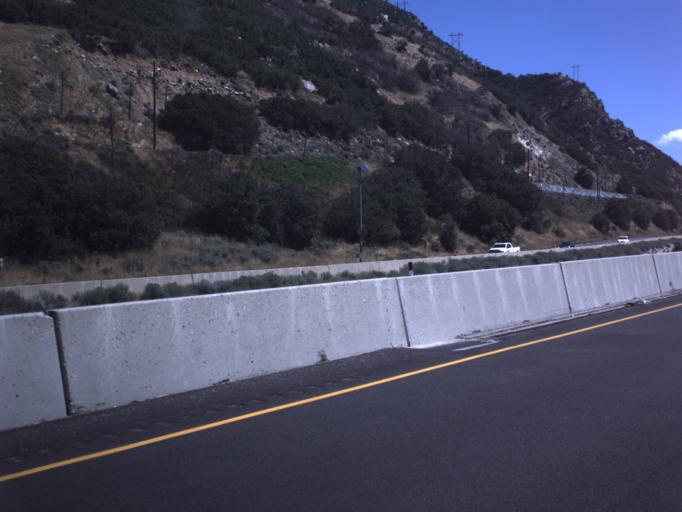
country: US
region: Utah
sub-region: Weber County
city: Uintah
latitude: 41.1380
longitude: -111.8724
